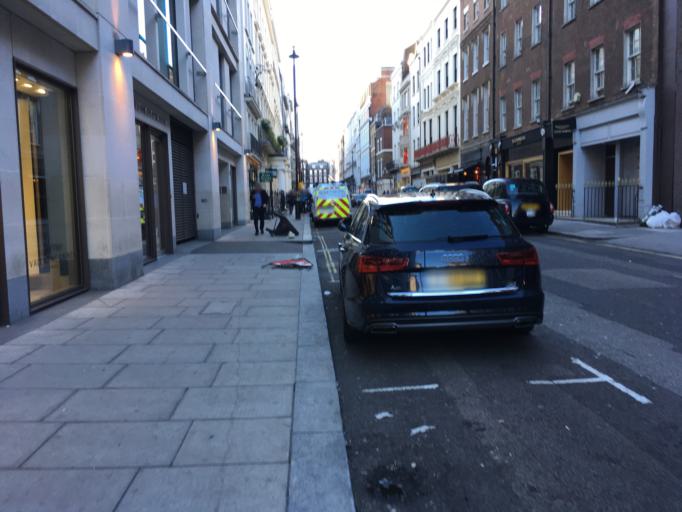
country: GB
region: England
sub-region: Greater London
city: London
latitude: 51.5078
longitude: -0.1415
